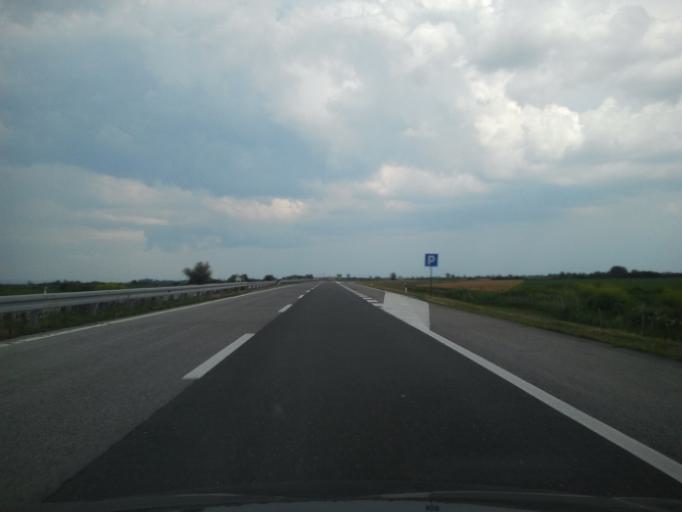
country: RS
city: Visnjicevo
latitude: 45.0410
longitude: 19.3612
